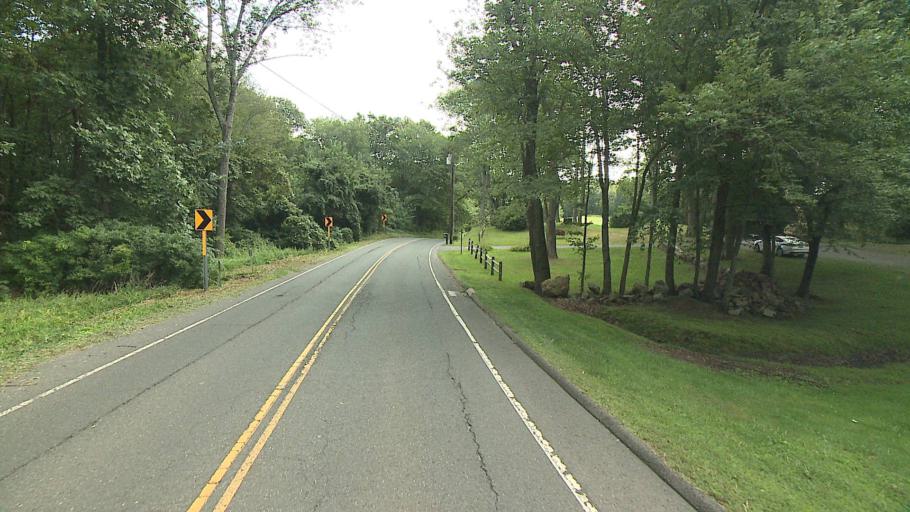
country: US
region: Connecticut
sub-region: Litchfield County
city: Bethlehem Village
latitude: 41.6491
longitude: -73.1661
